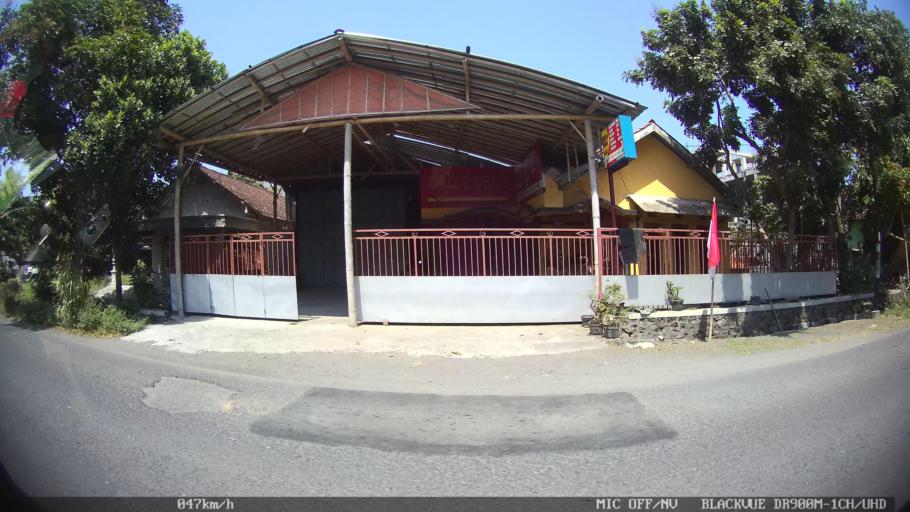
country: ID
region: Daerah Istimewa Yogyakarta
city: Srandakan
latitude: -7.9101
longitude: 110.0865
